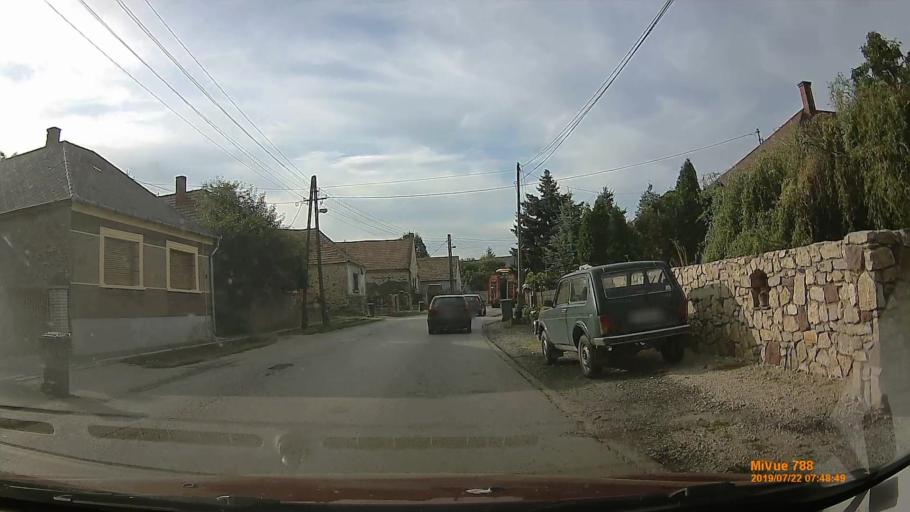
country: HU
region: Veszprem
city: Ajka
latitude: 47.0729
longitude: 17.5498
